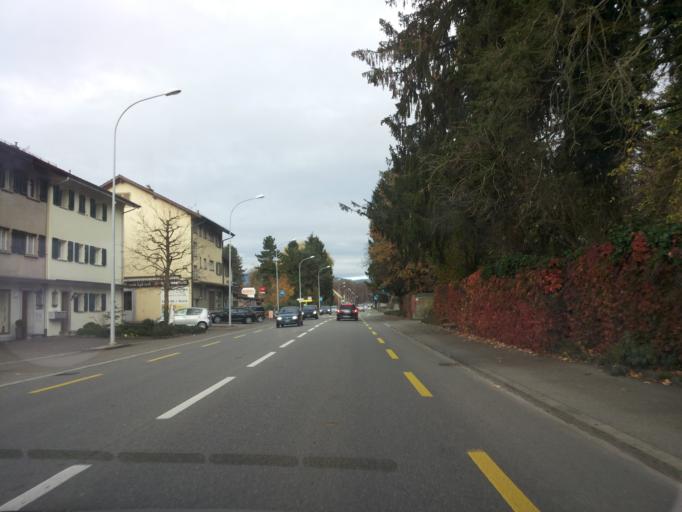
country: CH
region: Bern
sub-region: Oberaargau
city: Langenthal
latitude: 47.2200
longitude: 7.7835
